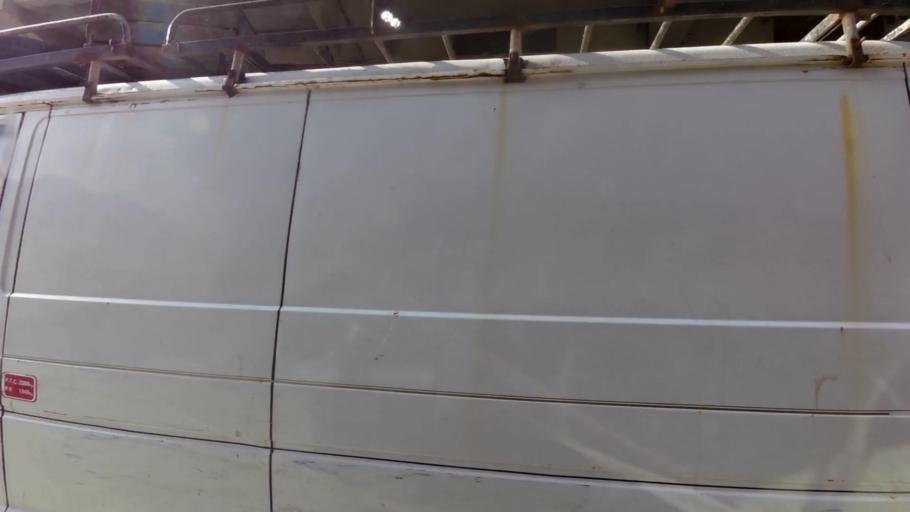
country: MA
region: Tanger-Tetouan
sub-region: Tetouan
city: Martil
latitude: 35.6110
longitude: -5.2751
